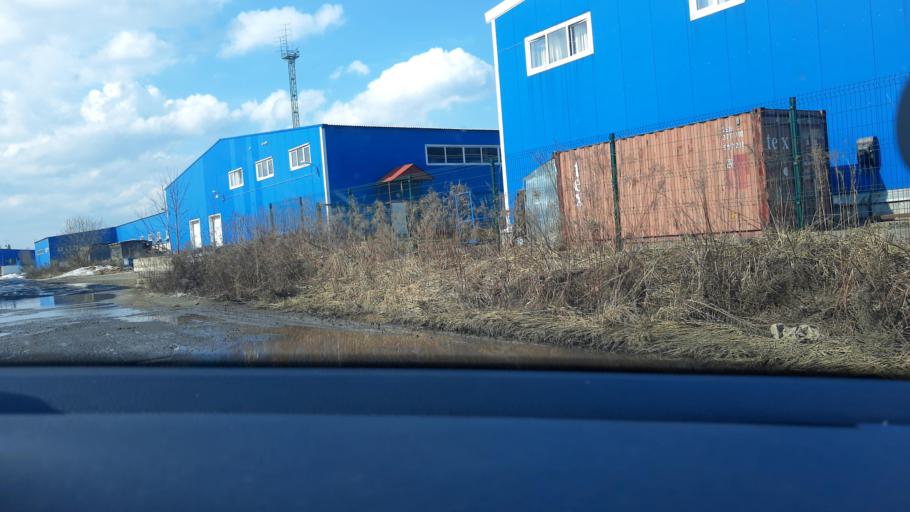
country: RU
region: Moskovskaya
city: Ivanteyevka
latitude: 55.9605
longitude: 37.8955
